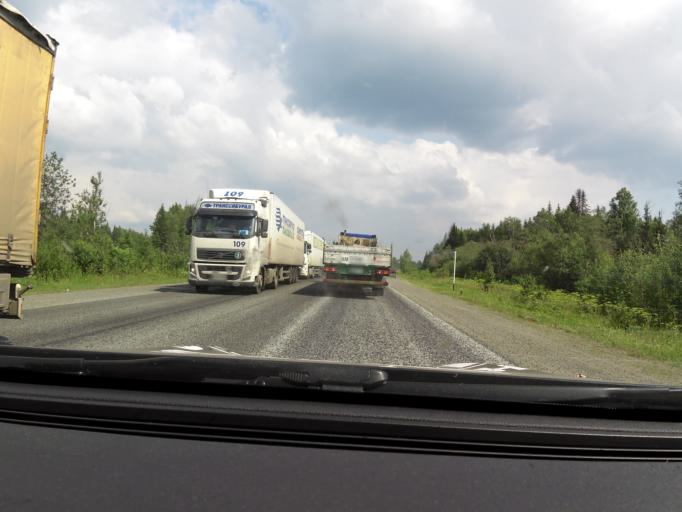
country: RU
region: Sverdlovsk
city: Ufimskiy
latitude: 56.7714
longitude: 58.1121
